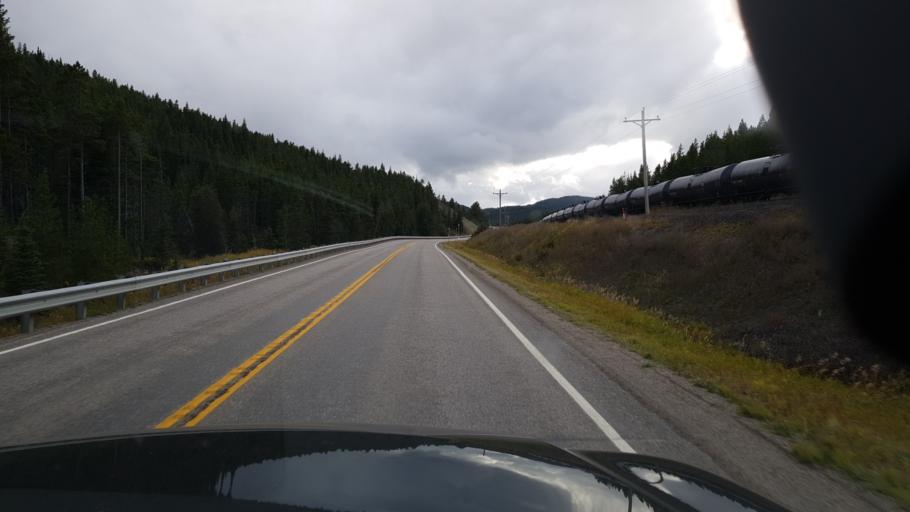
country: US
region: Montana
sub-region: Glacier County
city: South Browning
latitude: 48.3258
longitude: -113.3435
